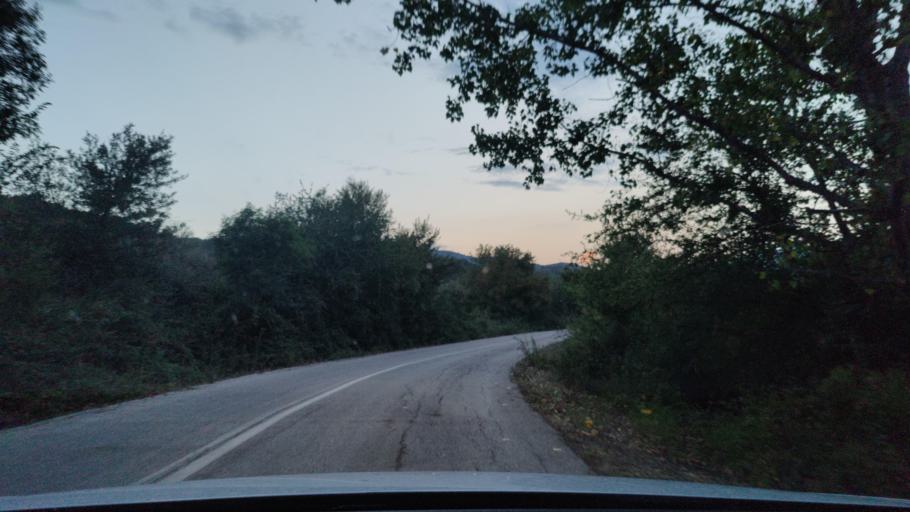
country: GR
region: Central Macedonia
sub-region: Nomos Serron
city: Chrysochorafa
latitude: 41.1592
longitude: 23.1906
